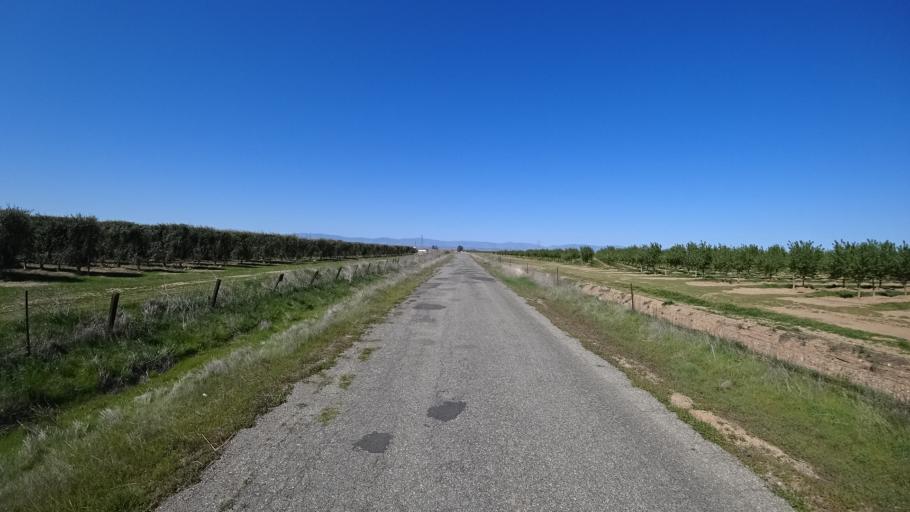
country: US
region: California
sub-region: Glenn County
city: Orland
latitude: 39.6538
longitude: -122.2559
